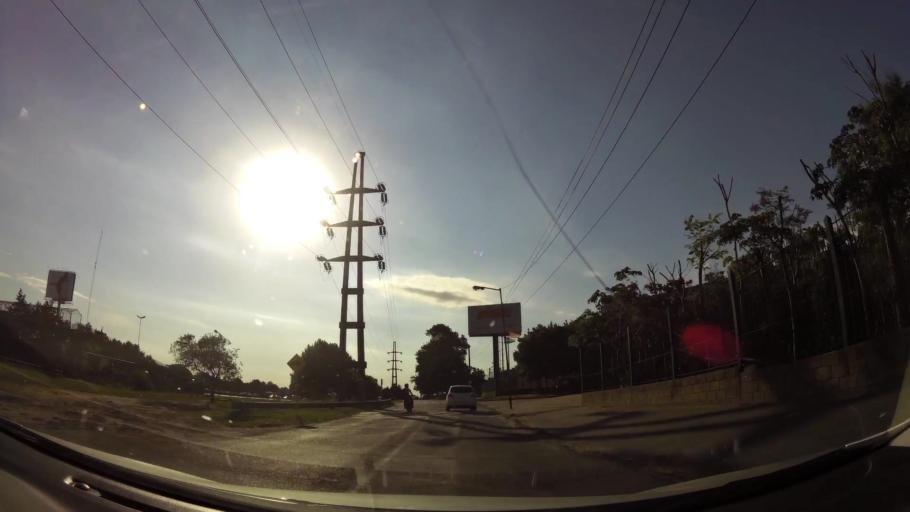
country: AR
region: Buenos Aires
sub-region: Partido de Tigre
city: Tigre
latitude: -34.4781
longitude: -58.6506
